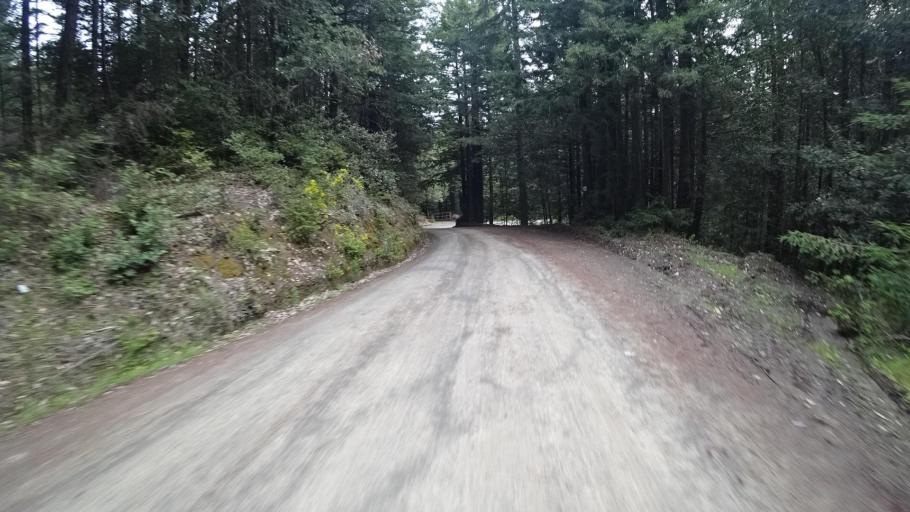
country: US
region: California
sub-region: Humboldt County
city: Redway
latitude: 40.3162
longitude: -123.8317
